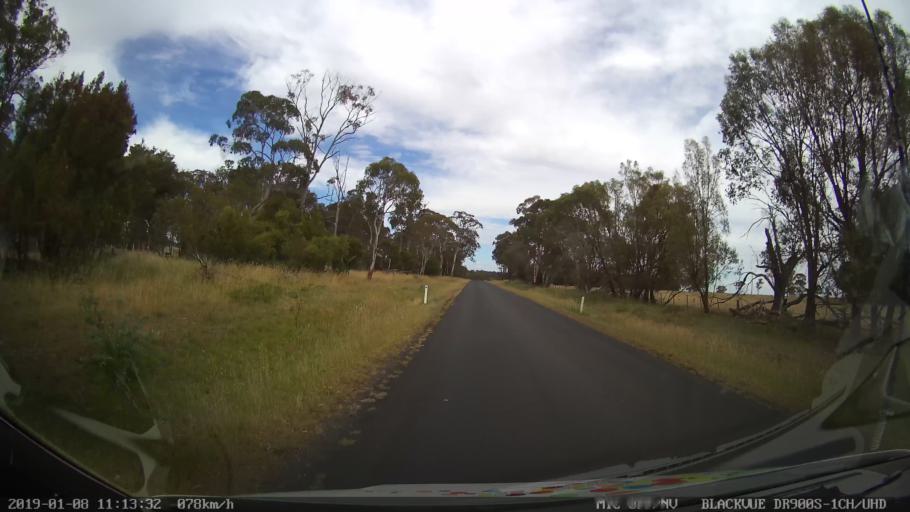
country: AU
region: New South Wales
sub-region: Guyra
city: Guyra
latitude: -30.2295
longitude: 151.5992
